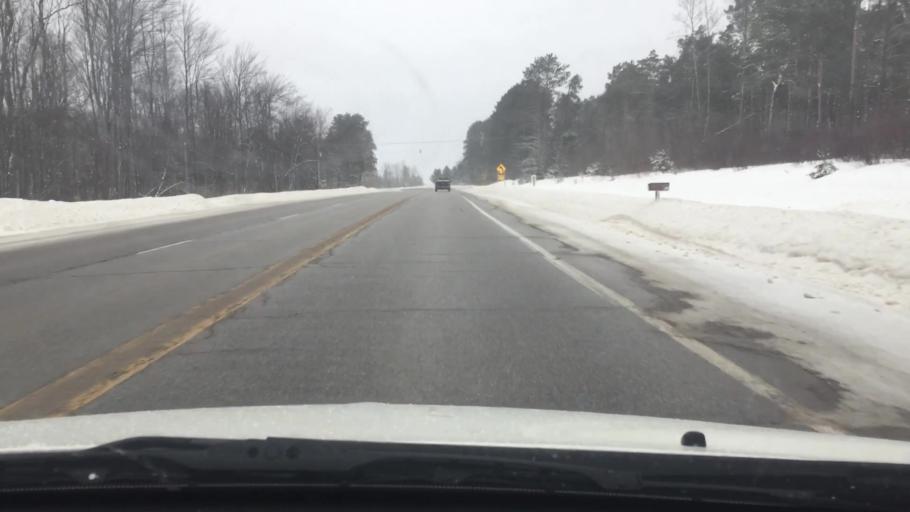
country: US
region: Michigan
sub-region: Otsego County
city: Gaylord
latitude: 45.0559
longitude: -84.7759
